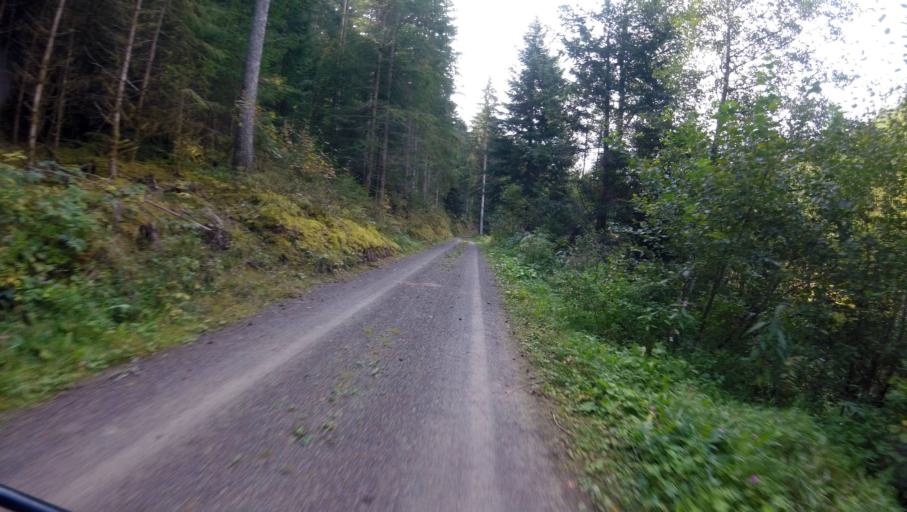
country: DE
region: Baden-Wuerttemberg
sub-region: Karlsruhe Region
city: Grombach
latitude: 48.5890
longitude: 8.5572
